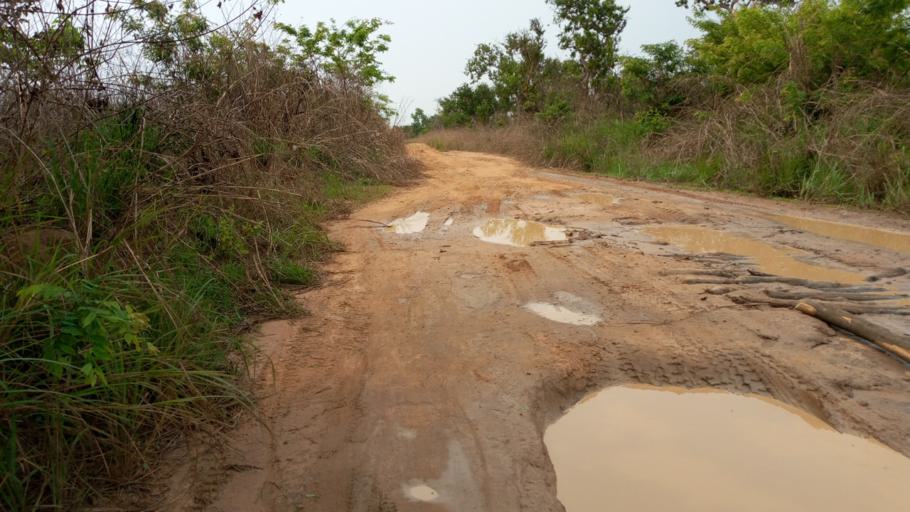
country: CD
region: Bandundu
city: Bandundu
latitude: -3.4636
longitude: 17.7715
